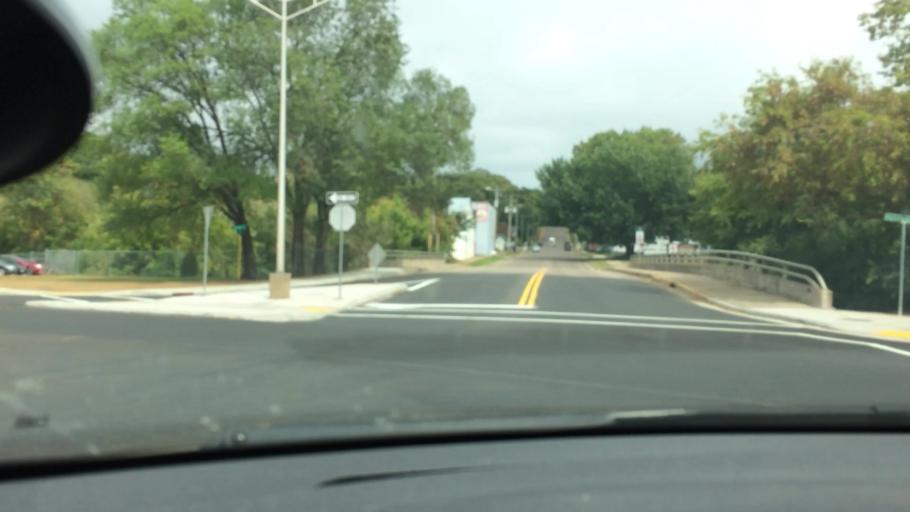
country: US
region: Wisconsin
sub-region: Chippewa County
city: Chippewa Falls
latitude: 44.9388
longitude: -91.3922
